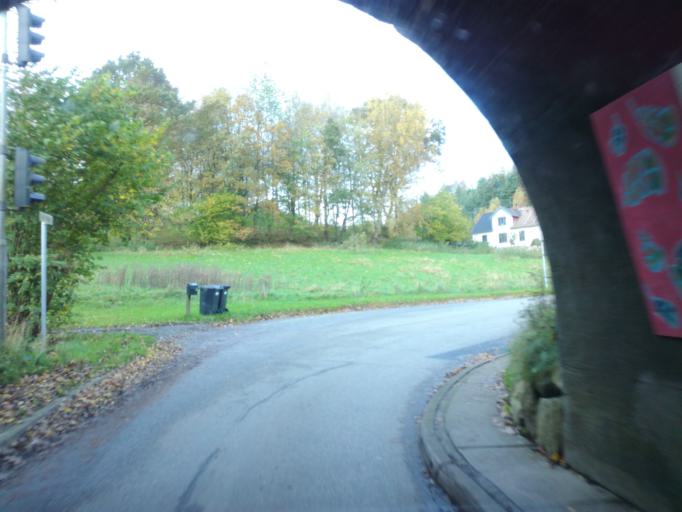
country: DK
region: South Denmark
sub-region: Vejle Kommune
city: Brejning
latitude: 55.6659
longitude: 9.6586
